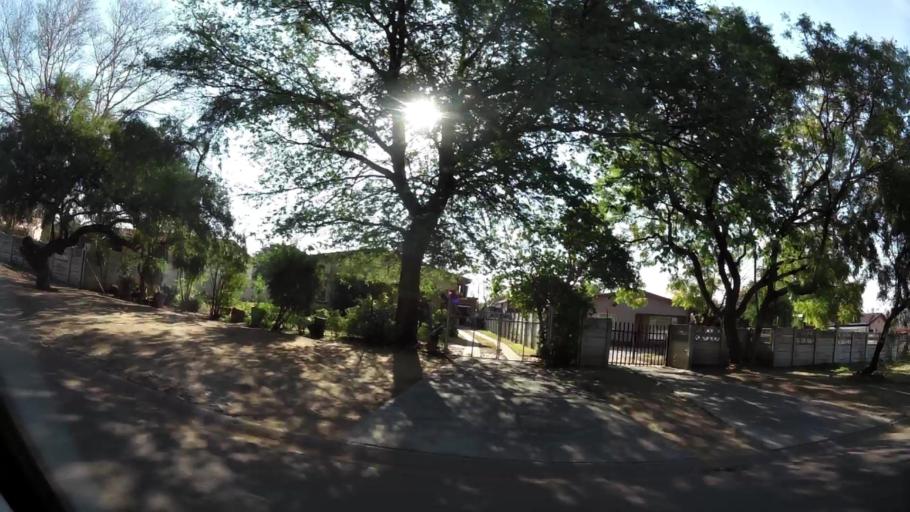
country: ZA
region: North-West
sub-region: Bojanala Platinum District Municipality
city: Rustenburg
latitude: -25.6583
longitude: 27.2632
